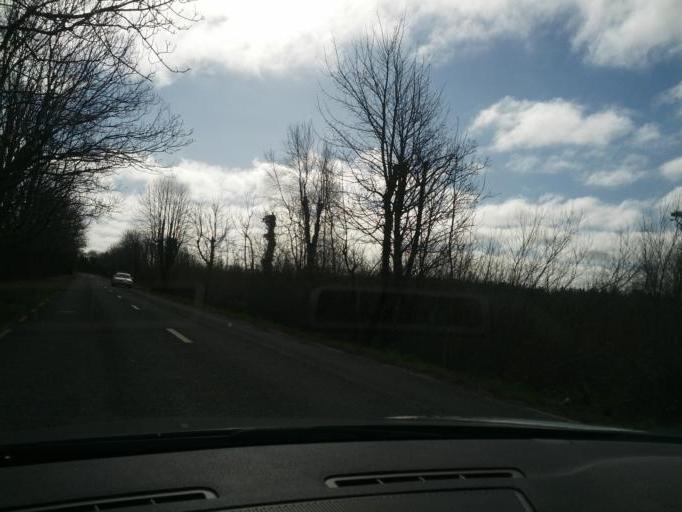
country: IE
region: Connaught
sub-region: County Galway
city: Ballinasloe
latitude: 53.4201
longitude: -8.3892
